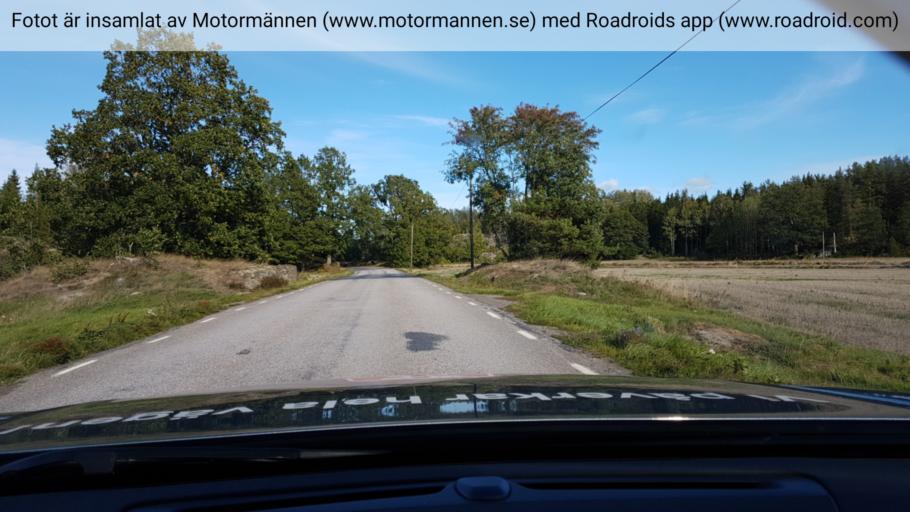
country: SE
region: OEstergoetland
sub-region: Valdemarsviks Kommun
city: Valdemarsvik
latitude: 58.0523
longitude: 16.6152
